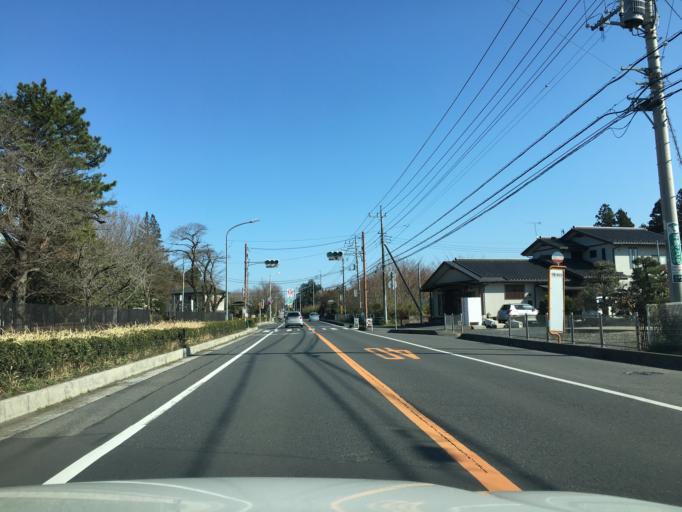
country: JP
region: Ibaraki
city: Omiya
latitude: 36.4749
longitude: 140.3851
